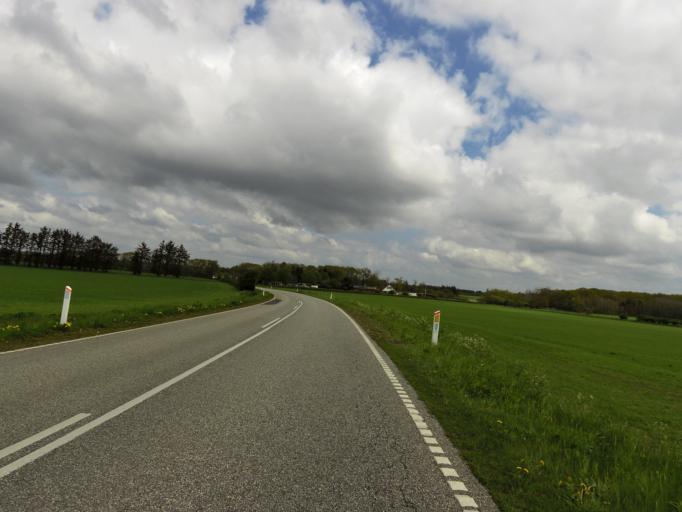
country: DK
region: South Denmark
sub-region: Haderslev Kommune
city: Gram
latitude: 55.2514
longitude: 8.9800
